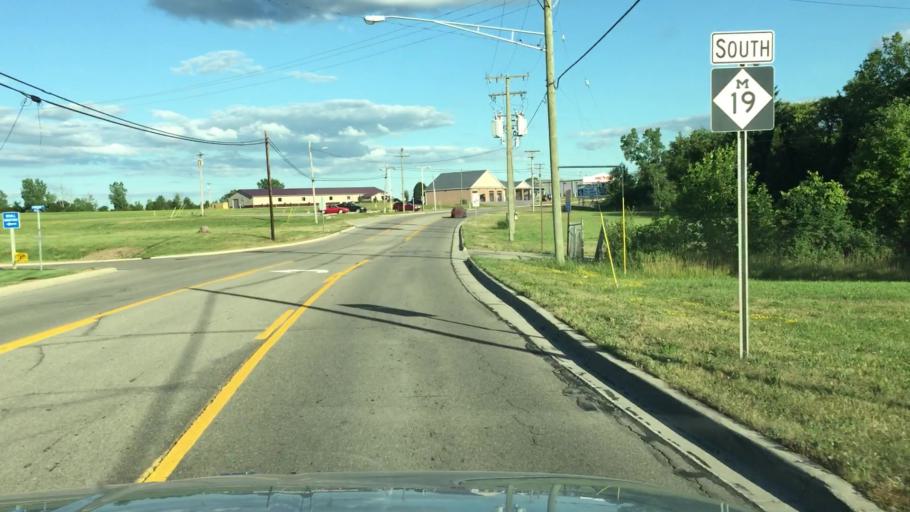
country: US
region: Michigan
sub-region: Saint Clair County
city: Yale
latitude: 43.1231
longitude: -82.7931
